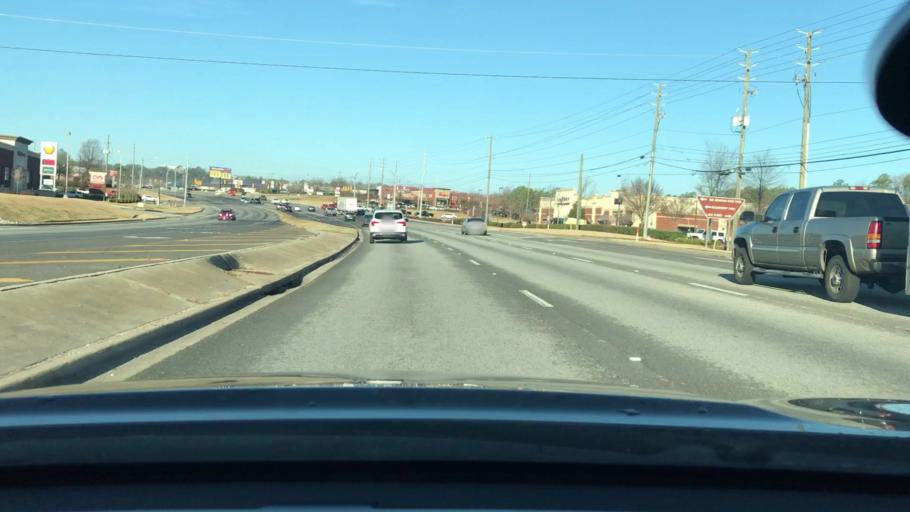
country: US
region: Alabama
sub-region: Shelby County
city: Lake Purdy
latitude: 33.4183
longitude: -86.6695
